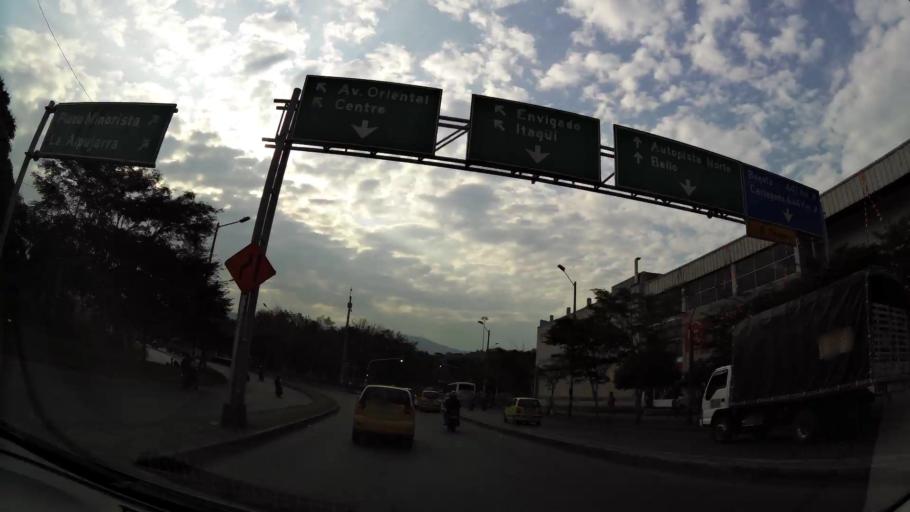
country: CO
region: Antioquia
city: Medellin
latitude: 6.2587
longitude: -75.5710
